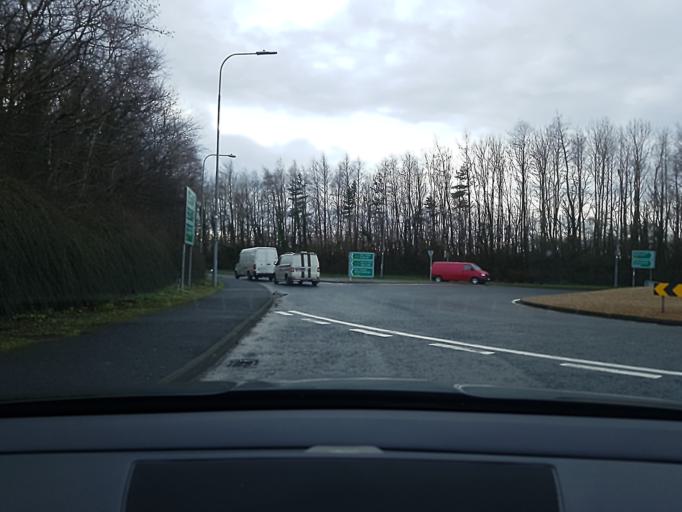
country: IE
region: Connaught
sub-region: Maigh Eo
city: Castlebar
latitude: 53.8489
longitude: -9.3086
